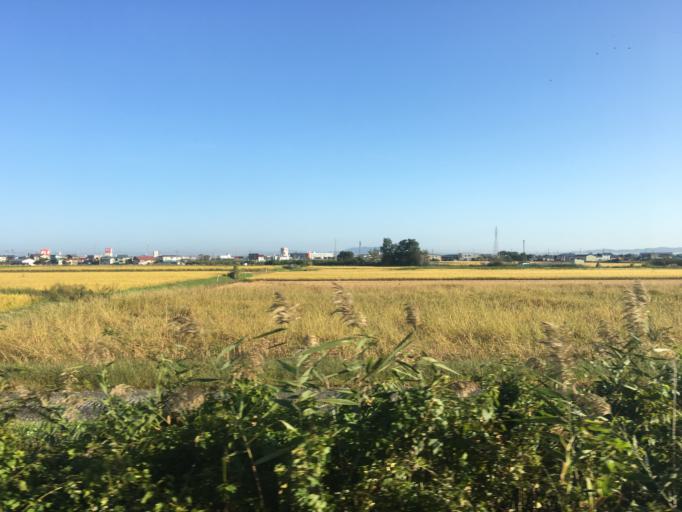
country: JP
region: Aomori
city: Hirosaki
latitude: 40.5883
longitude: 140.5127
